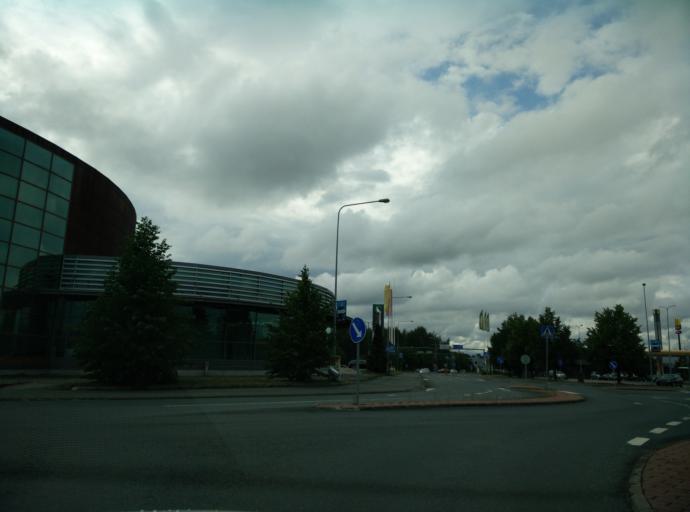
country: FI
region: Haeme
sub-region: Haemeenlinna
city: Haemeenlinna
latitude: 61.0074
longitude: 24.4196
